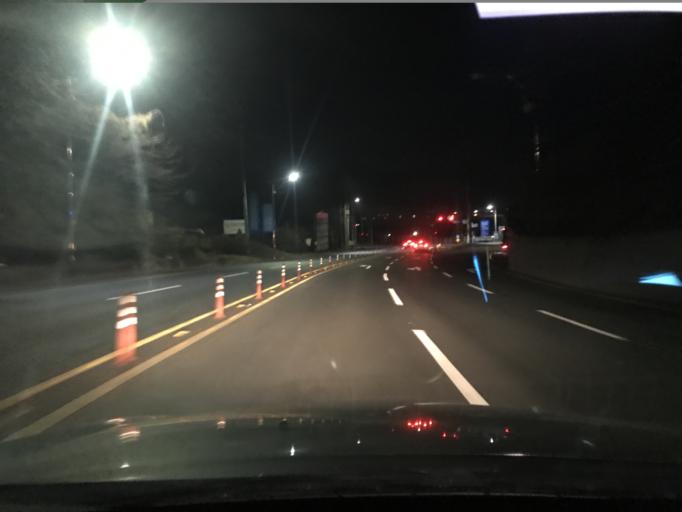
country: KR
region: Daegu
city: Hwawon
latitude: 35.7297
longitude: 128.4655
